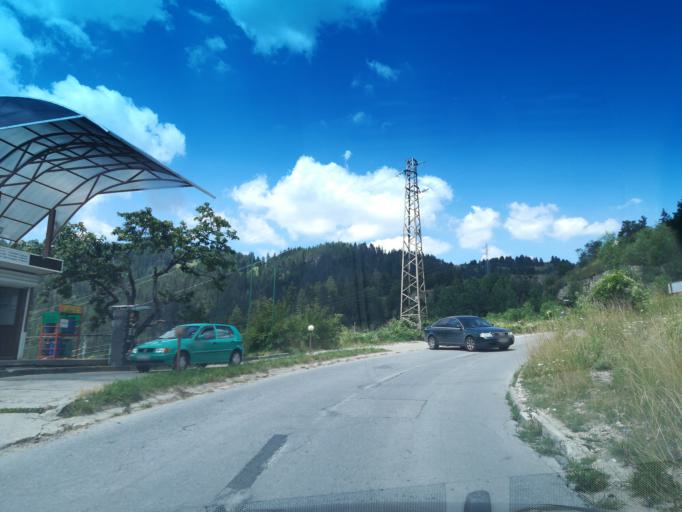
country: BG
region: Smolyan
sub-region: Obshtina Chepelare
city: Chepelare
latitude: 41.6655
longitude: 24.7753
